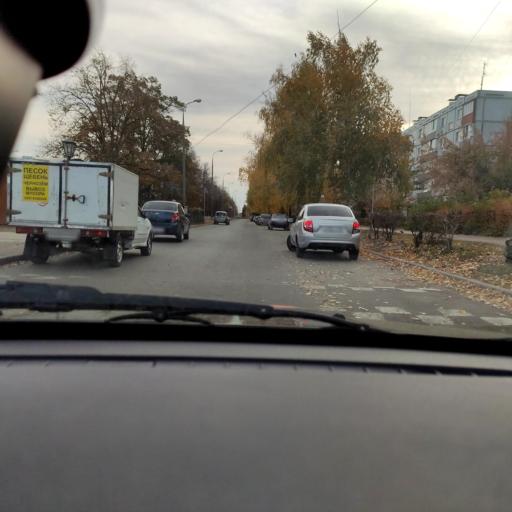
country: RU
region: Samara
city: Tol'yatti
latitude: 53.5299
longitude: 49.2665
